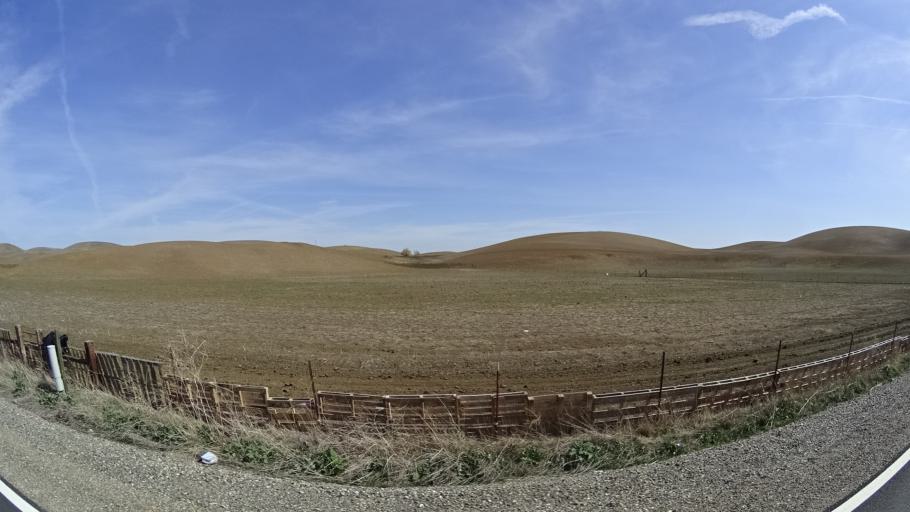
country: US
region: California
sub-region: Glenn County
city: Willows
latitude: 39.5476
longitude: -122.3518
